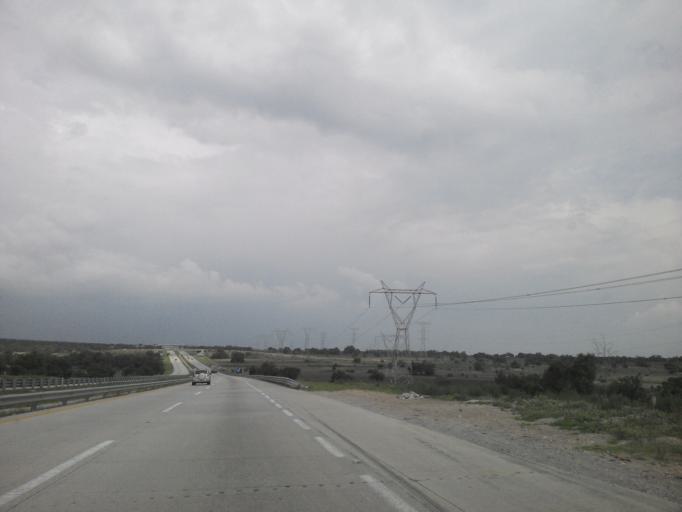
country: MX
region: Mexico
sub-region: Apaxco
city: Colonia Juarez
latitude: 19.9952
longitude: -99.1350
